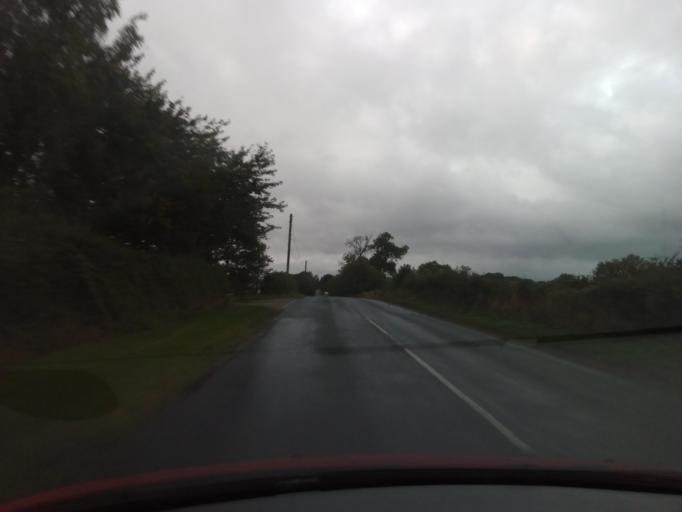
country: GB
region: England
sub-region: Darlington
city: High Coniscliffe
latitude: 54.4861
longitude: -1.6702
